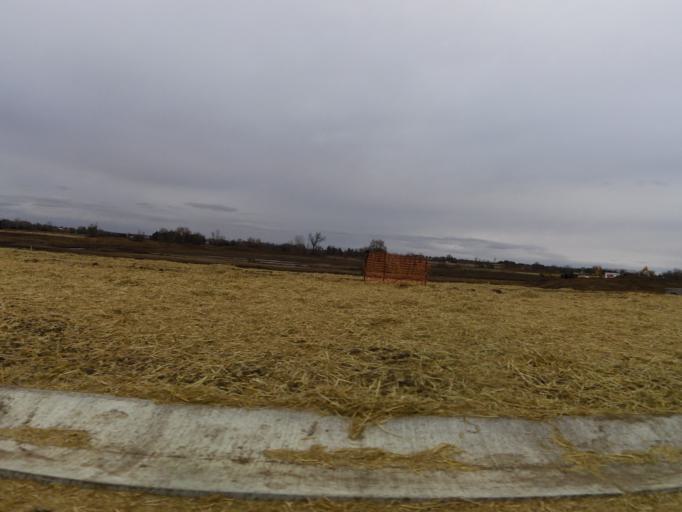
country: US
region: Minnesota
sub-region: Washington County
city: Lake Elmo
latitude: 44.9977
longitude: -92.8683
